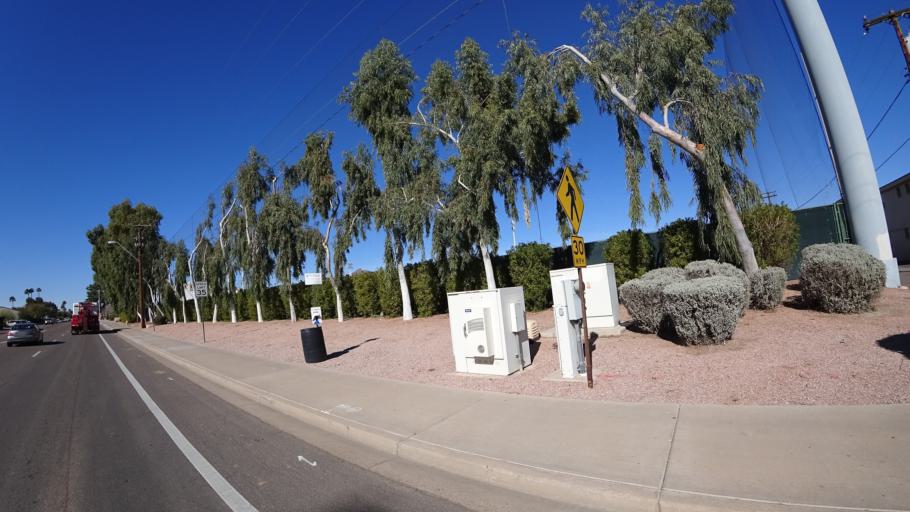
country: US
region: Arizona
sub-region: Maricopa County
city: Scottsdale
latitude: 33.4877
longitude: -111.9188
